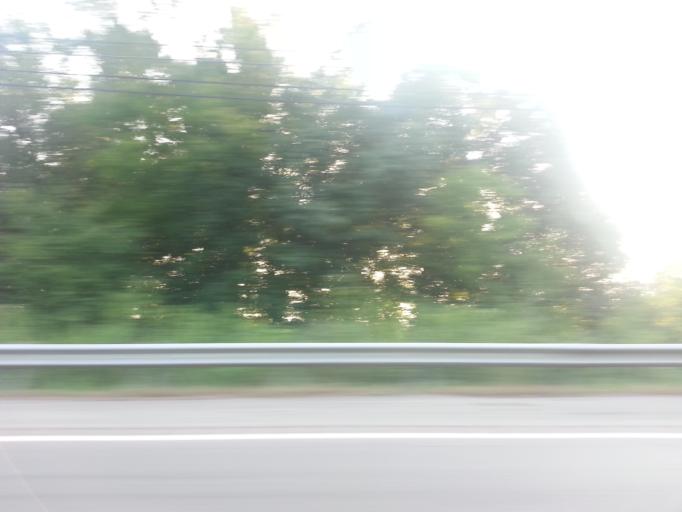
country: US
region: Tennessee
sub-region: McMinn County
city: Athens
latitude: 35.4888
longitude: -84.5999
